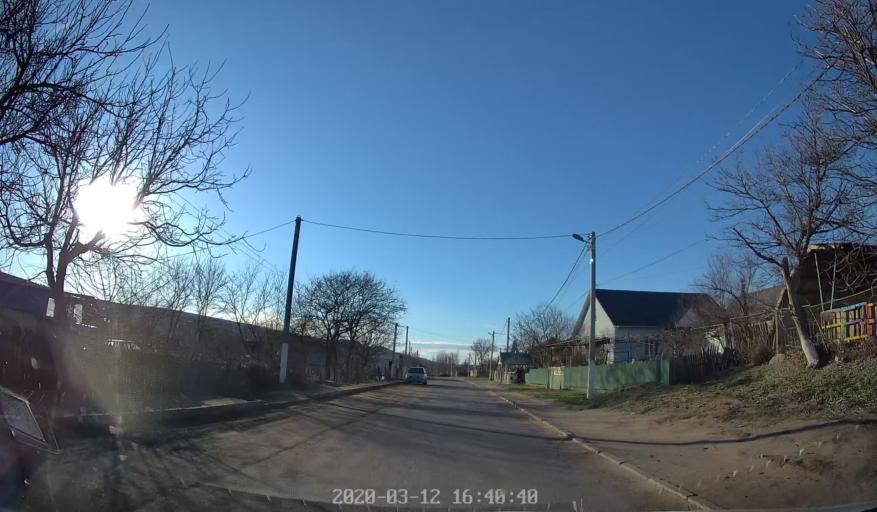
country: MD
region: Anenii Noi
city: Anenii Noi
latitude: 46.8189
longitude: 29.1451
